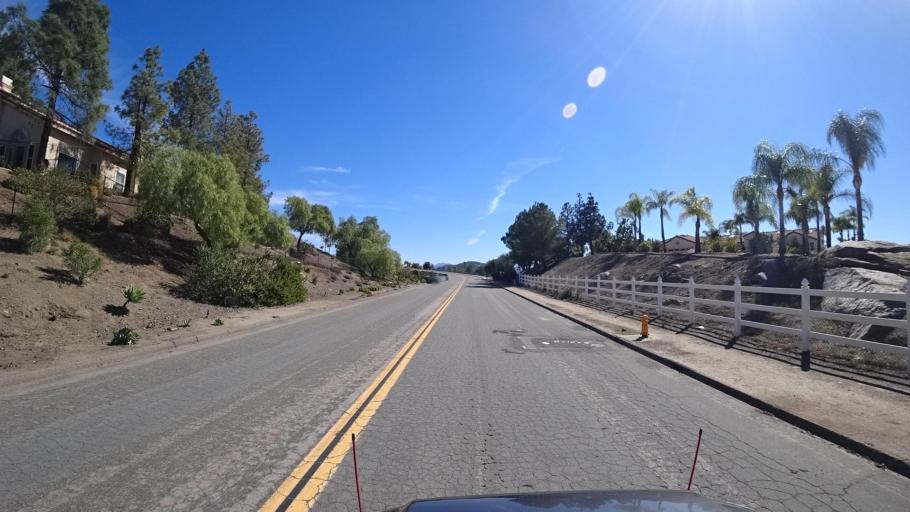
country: US
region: California
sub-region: San Diego County
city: Harbison Canyon
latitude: 32.8753
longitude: -116.8346
